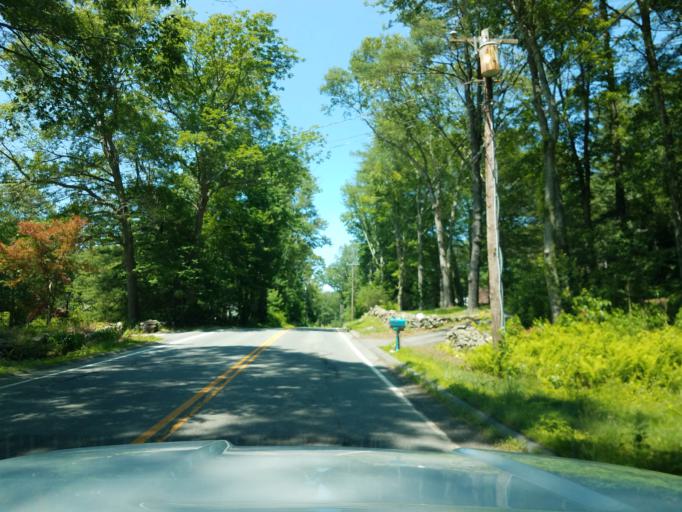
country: US
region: Connecticut
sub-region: Windham County
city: Killingly Center
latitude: 41.8859
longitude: -71.8683
